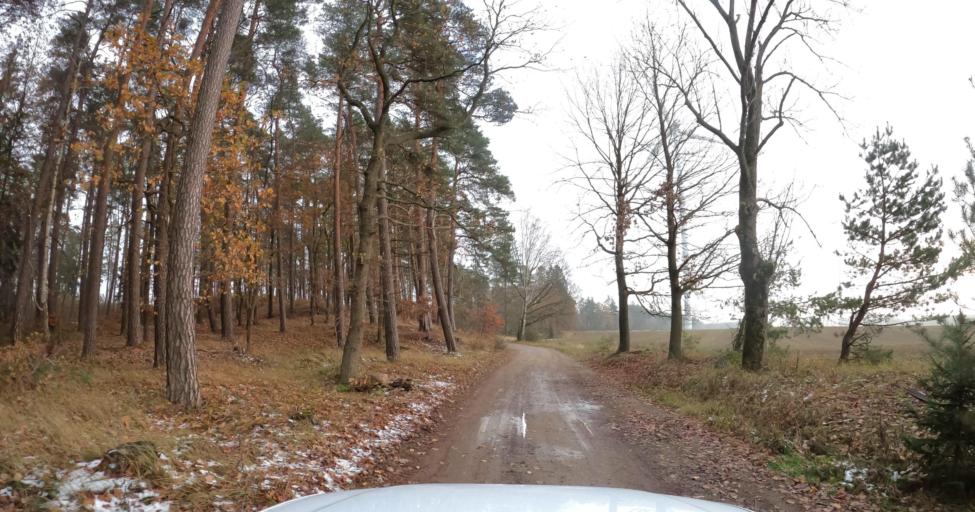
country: PL
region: West Pomeranian Voivodeship
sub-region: Powiat bialogardzki
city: Karlino
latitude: 53.9259
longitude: 15.8365
